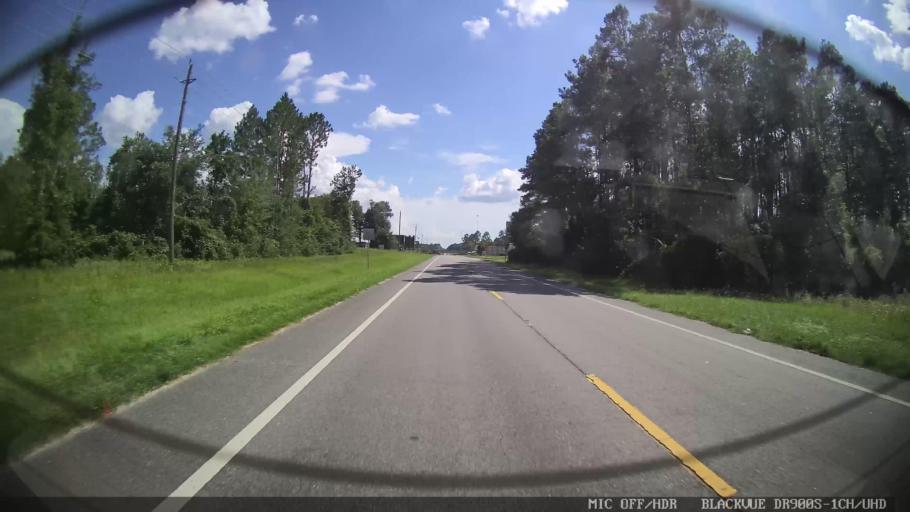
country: US
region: Florida
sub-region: Hamilton County
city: Jasper
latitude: 30.5296
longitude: -83.0488
